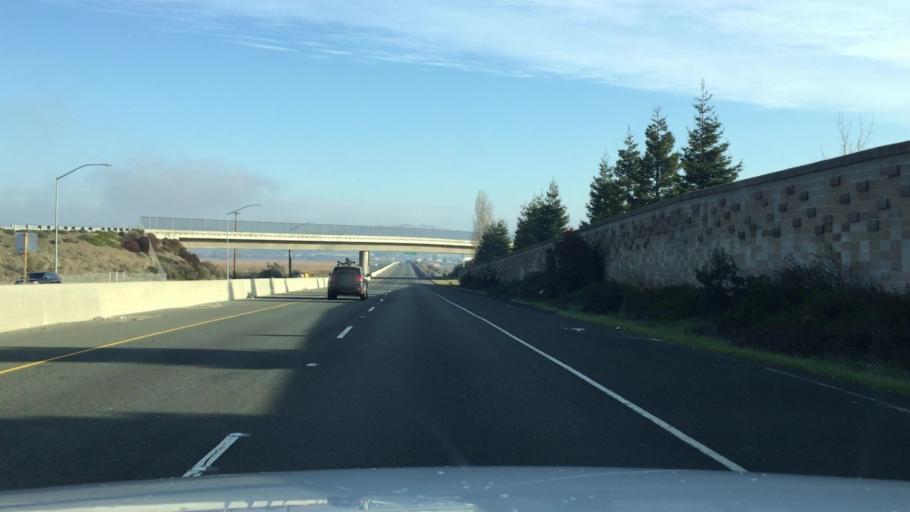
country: US
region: California
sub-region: Solano County
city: Vallejo
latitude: 38.1249
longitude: -122.2702
